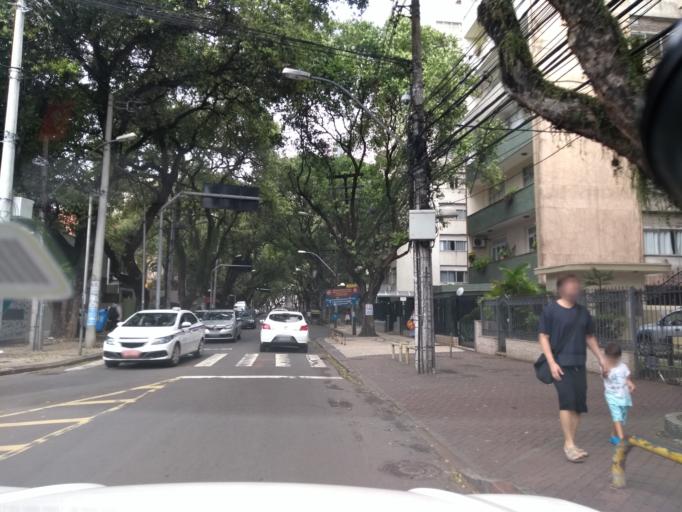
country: BR
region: Bahia
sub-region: Salvador
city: Salvador
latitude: -12.9889
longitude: -38.5234
